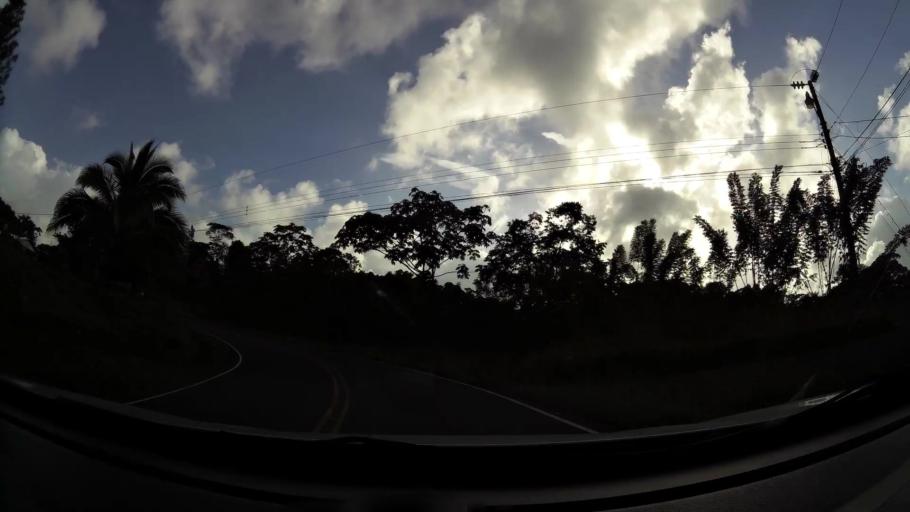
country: CR
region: Limon
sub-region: Canton de Siquirres
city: Siquirres
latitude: 10.0691
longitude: -83.5536
